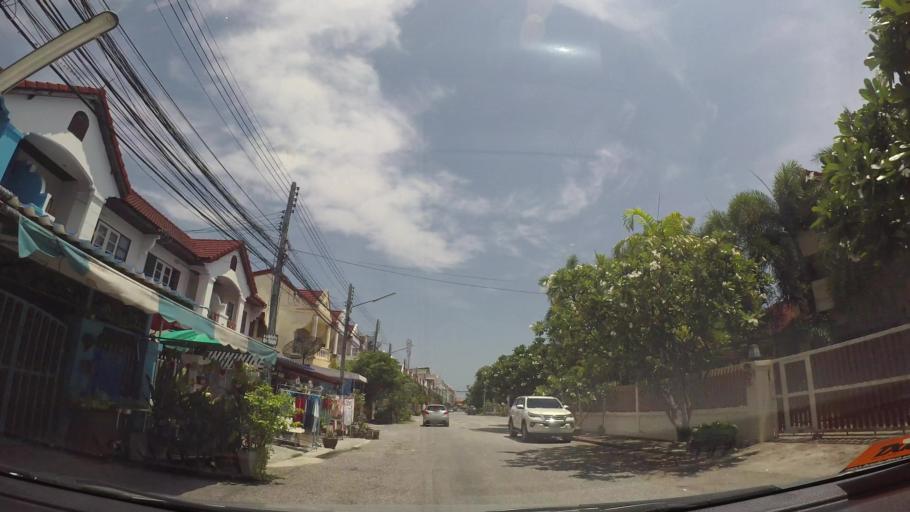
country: TH
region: Chon Buri
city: Chon Buri
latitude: 13.3325
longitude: 100.9380
